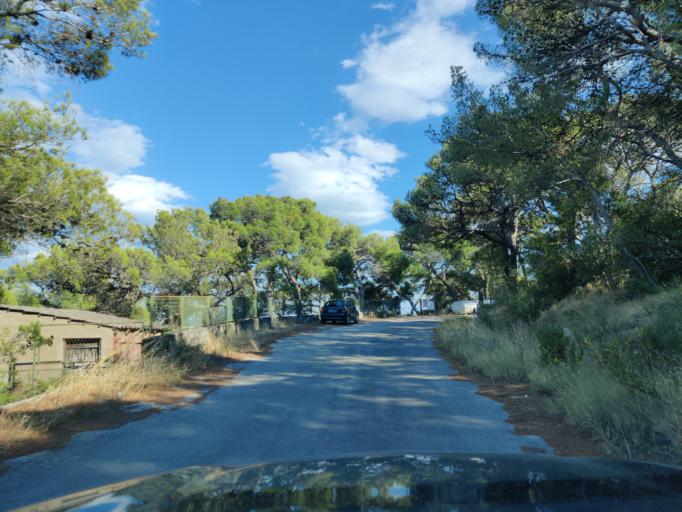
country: HR
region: Sibensko-Kniniska
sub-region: Grad Sibenik
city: Sibenik
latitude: 43.7368
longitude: 15.8760
